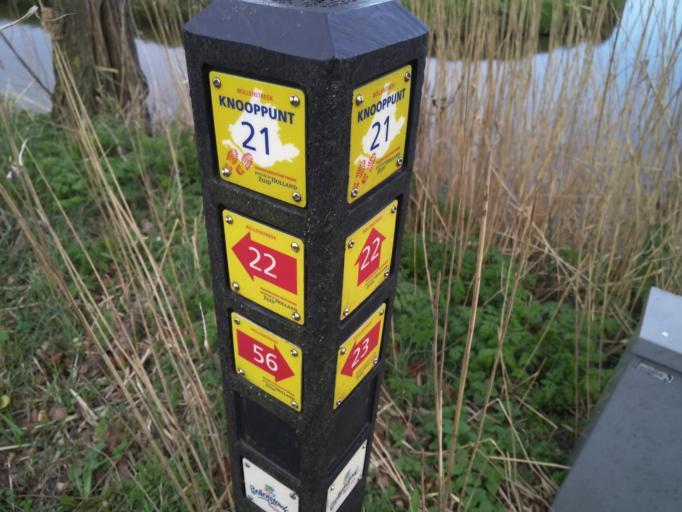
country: NL
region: South Holland
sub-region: Gemeente Teylingen
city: Sassenheim
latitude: 52.2465
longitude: 4.5354
